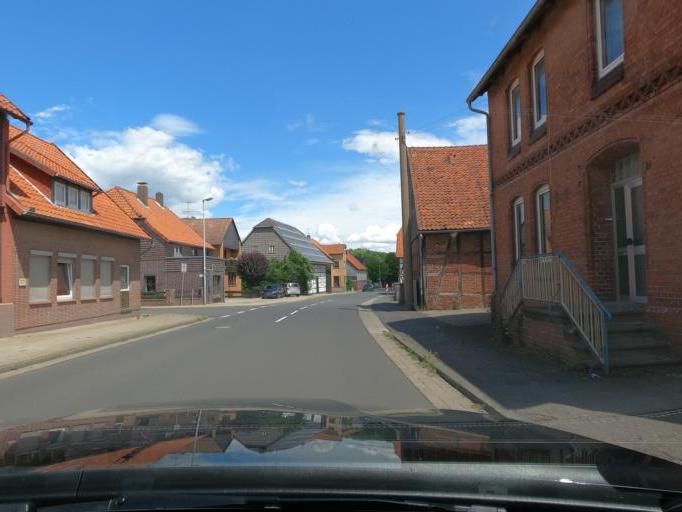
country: DE
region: Lower Saxony
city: Schellerten
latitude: 52.1740
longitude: 10.1335
